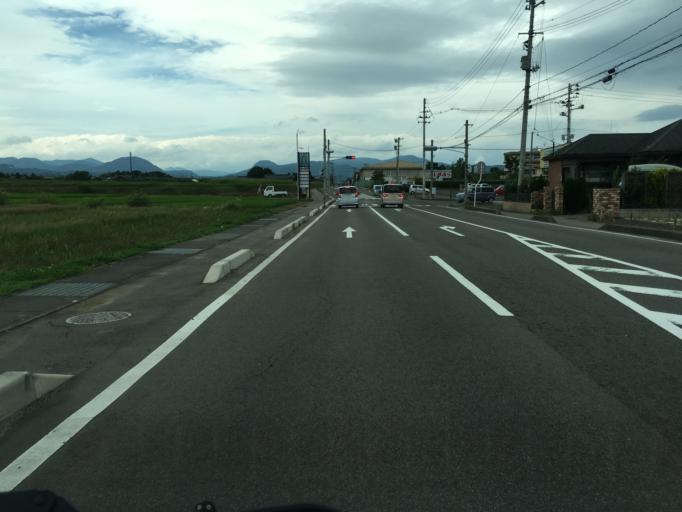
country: JP
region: Fukushima
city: Fukushima-shi
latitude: 37.7704
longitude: 140.4342
